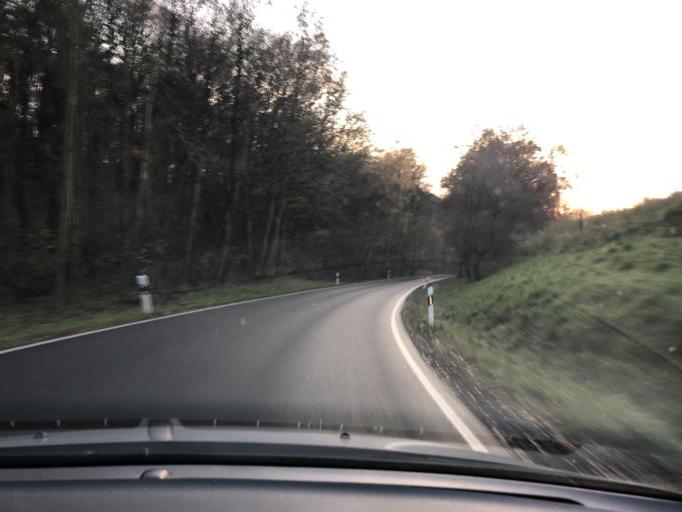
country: DE
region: Saxony
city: Nerchau
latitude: 51.2598
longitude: 12.7909
